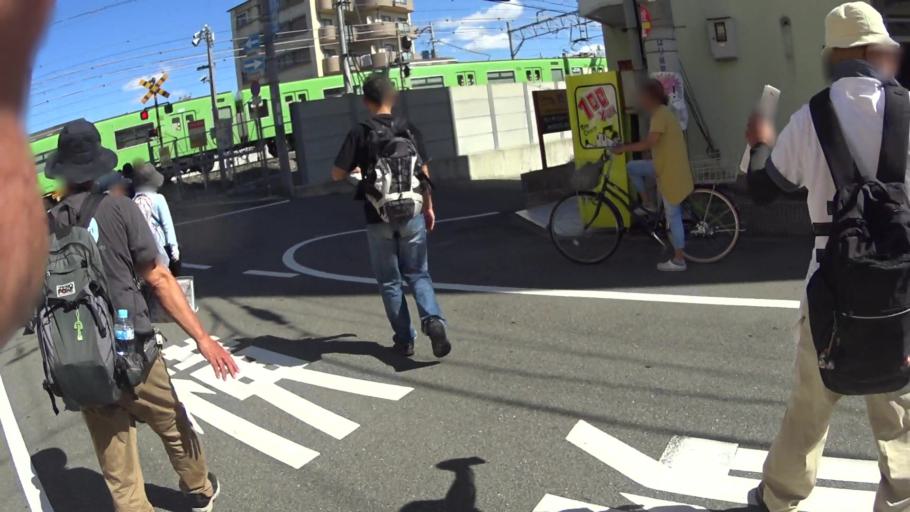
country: JP
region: Osaka
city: Yao
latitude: 34.6293
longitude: 135.5563
